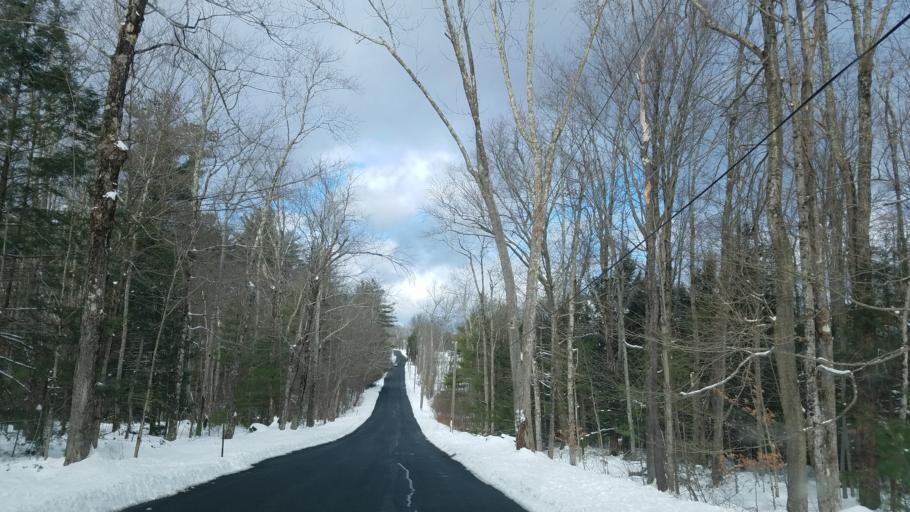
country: US
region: Connecticut
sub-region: Litchfield County
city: Winsted
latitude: 41.9759
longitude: -73.0800
